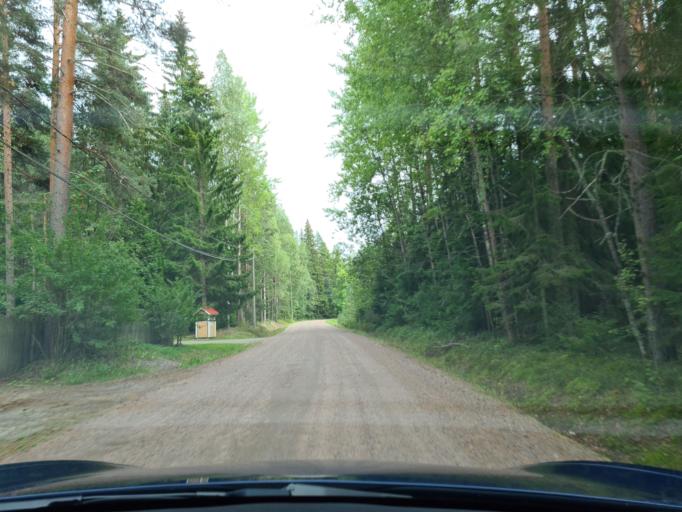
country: FI
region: Uusimaa
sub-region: Helsinki
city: Vihti
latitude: 60.4204
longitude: 24.4788
